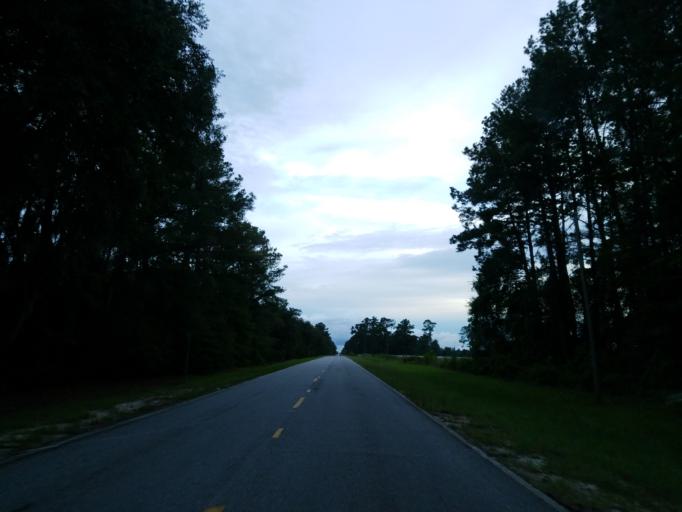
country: US
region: Georgia
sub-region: Echols County
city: Statenville
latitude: 30.6617
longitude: -83.0259
